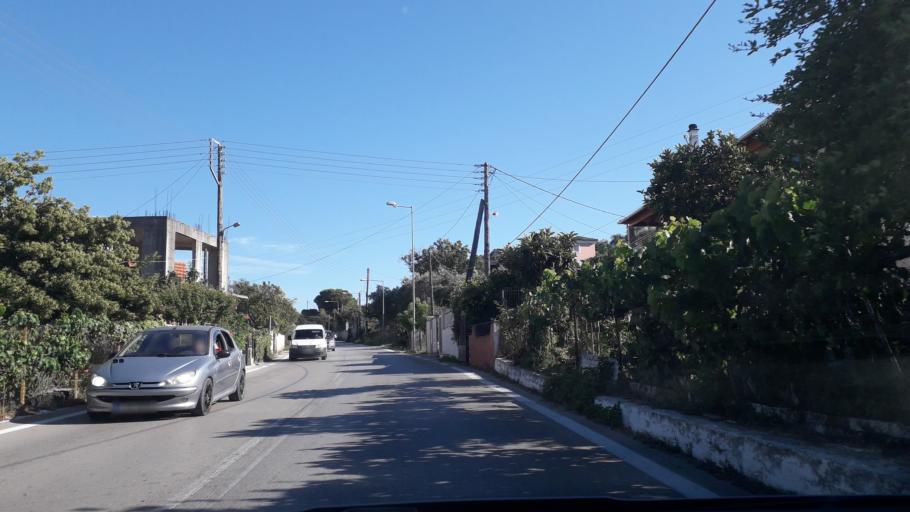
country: GR
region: Ionian Islands
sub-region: Nomos Kerkyras
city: Agios Matthaios
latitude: 39.4661
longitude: 19.9126
